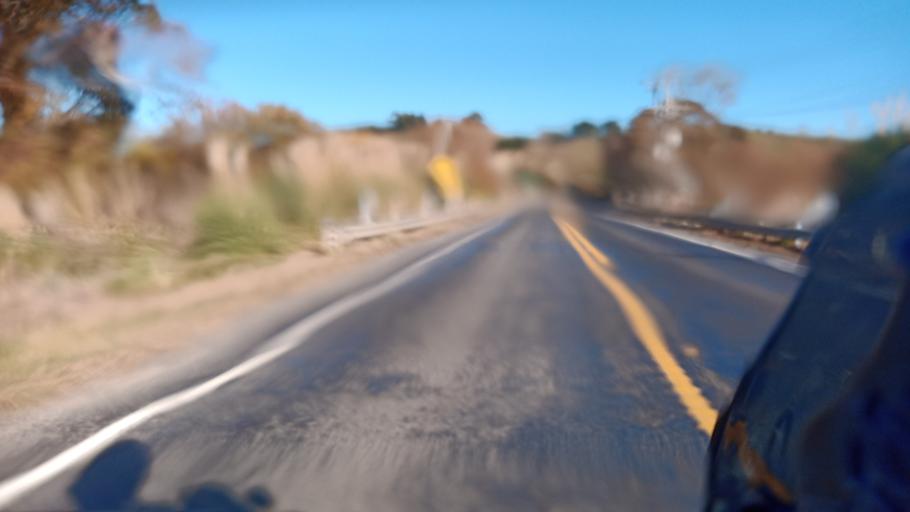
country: NZ
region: Hawke's Bay
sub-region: Napier City
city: Napier
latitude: -39.3933
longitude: 176.8792
